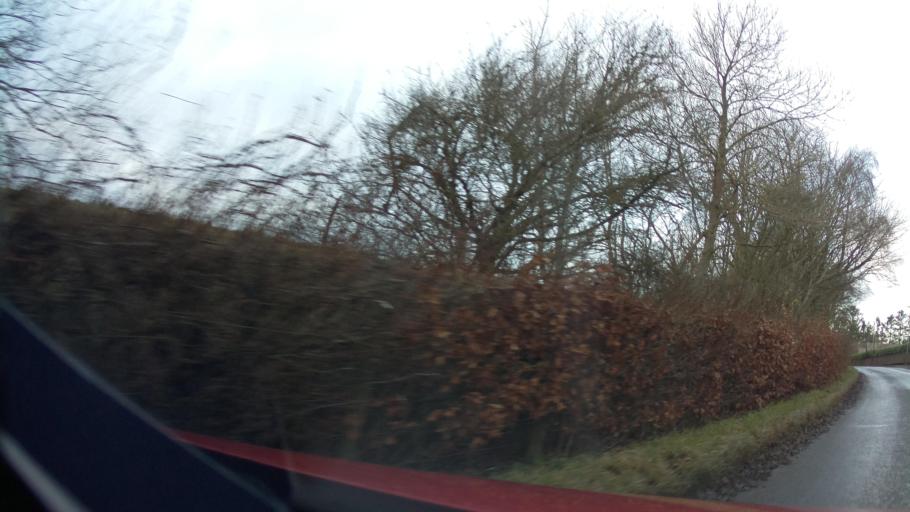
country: GB
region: Scotland
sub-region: Angus
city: Letham
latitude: 56.5313
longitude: -2.7970
